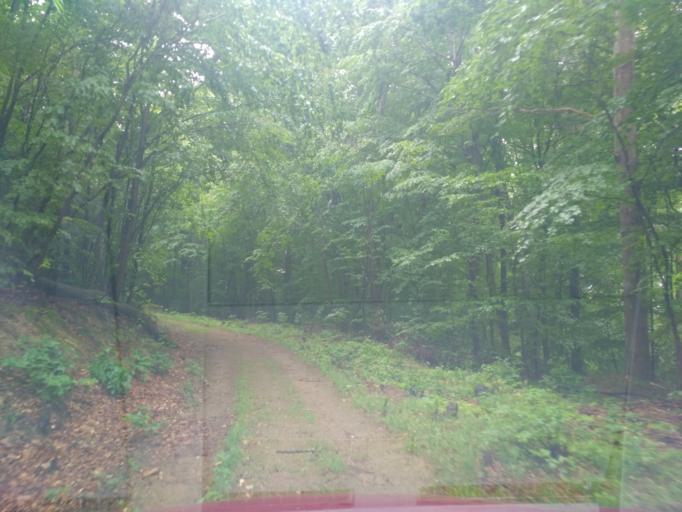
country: SK
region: Kosicky
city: Moldava nad Bodvou
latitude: 48.6973
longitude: 21.0721
